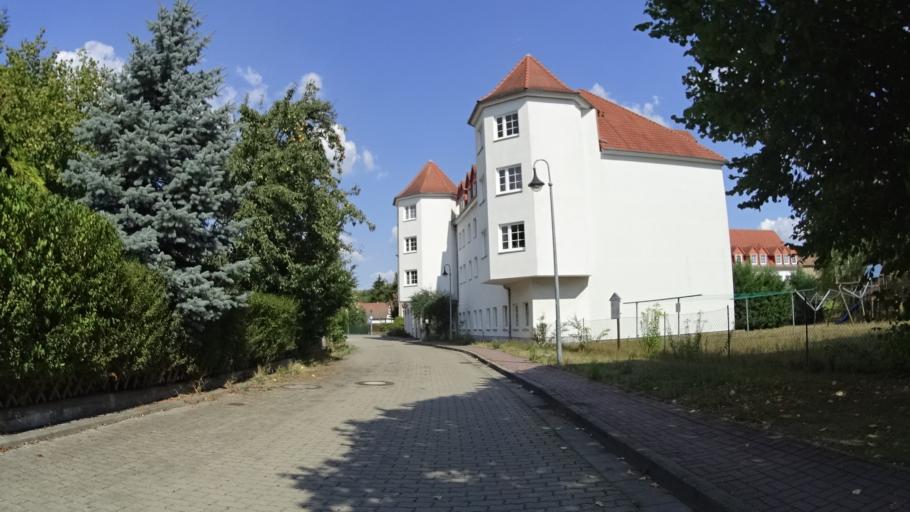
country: DE
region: Saxony
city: Hirschfelde
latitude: 50.9457
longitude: 14.8869
